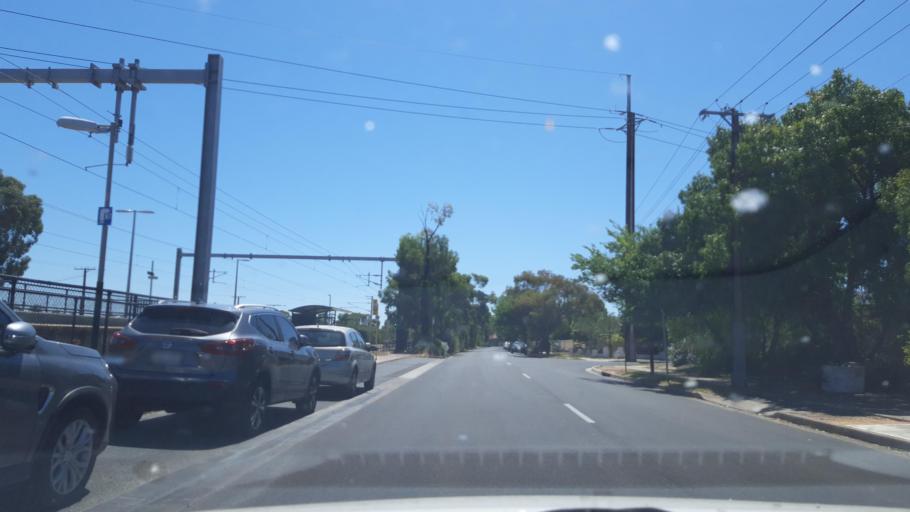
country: AU
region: South Australia
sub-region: Marion
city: South Plympton
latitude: -34.9828
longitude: 138.5675
